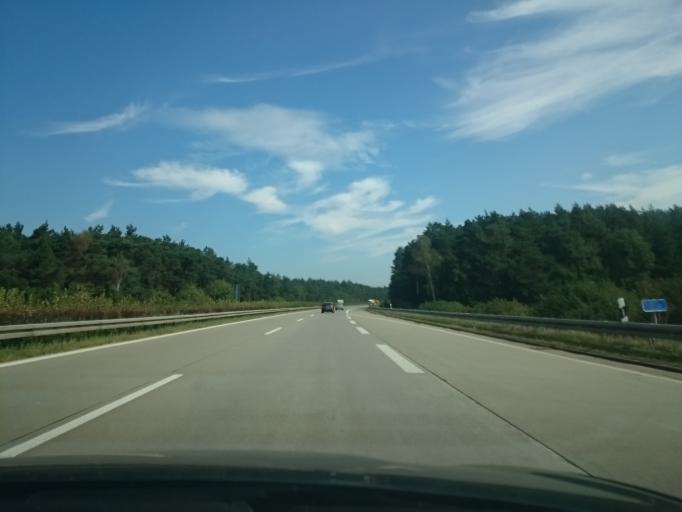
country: DE
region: Brandenburg
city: Ortrand
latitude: 51.3881
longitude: 13.7517
